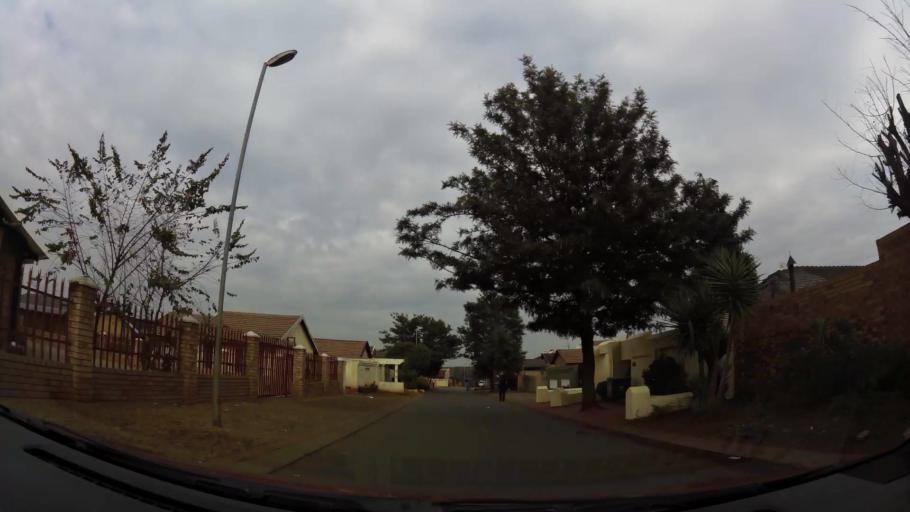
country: ZA
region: Gauteng
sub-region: City of Johannesburg Metropolitan Municipality
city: Soweto
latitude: -26.2707
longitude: 27.8283
